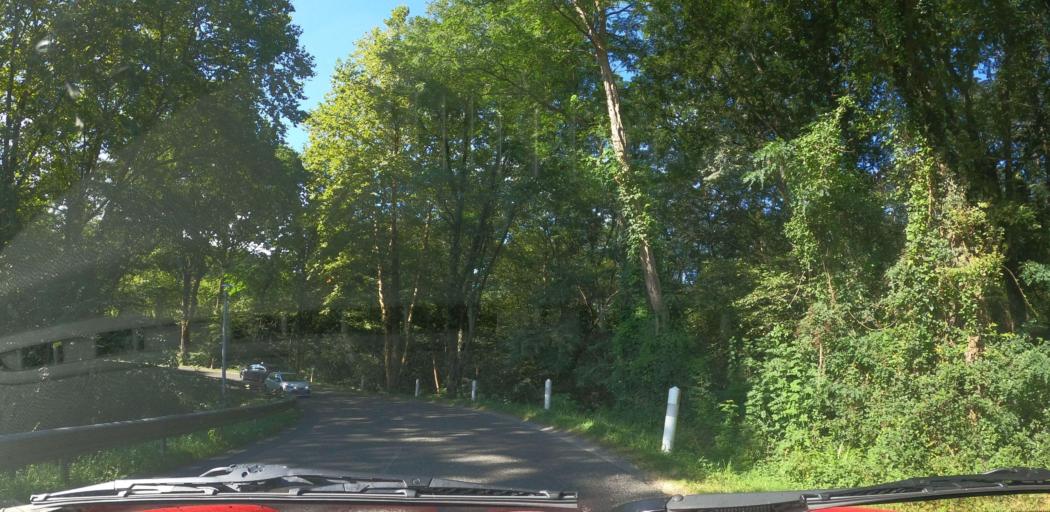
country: FR
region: Aquitaine
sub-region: Departement des Pyrenees-Atlantiques
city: Saint-Pee-sur-Nivelle
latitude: 43.3701
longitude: -1.5461
